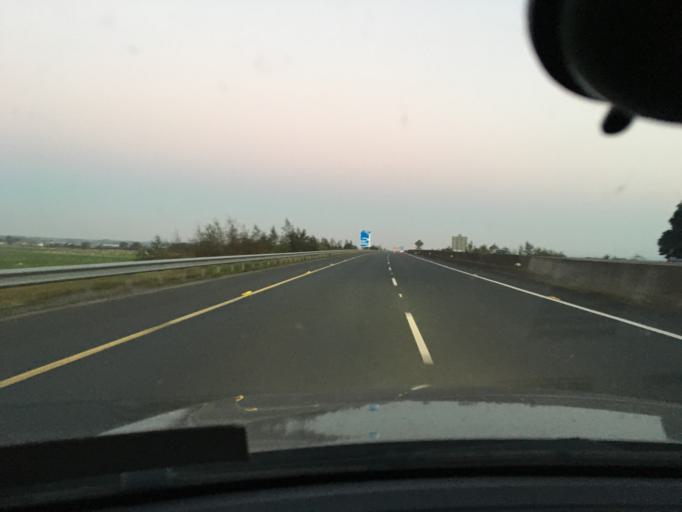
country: IE
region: Connaught
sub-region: County Galway
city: Athenry
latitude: 53.2933
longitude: -8.7765
